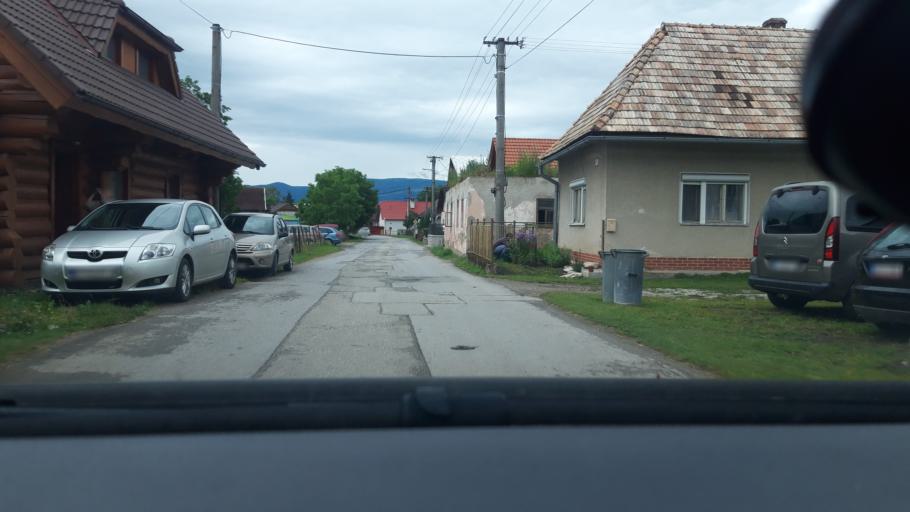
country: SK
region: Zilinsky
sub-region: Okres Martin
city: Martin
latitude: 49.0018
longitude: 18.9832
